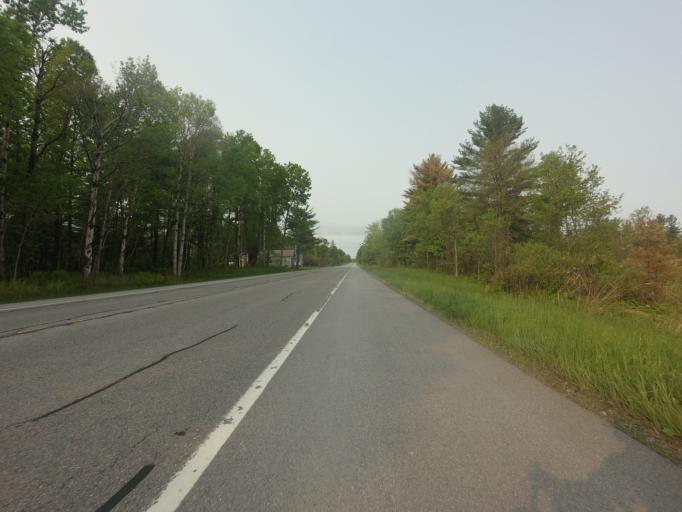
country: US
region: New York
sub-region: Jefferson County
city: Carthage
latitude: 44.0648
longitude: -75.5324
